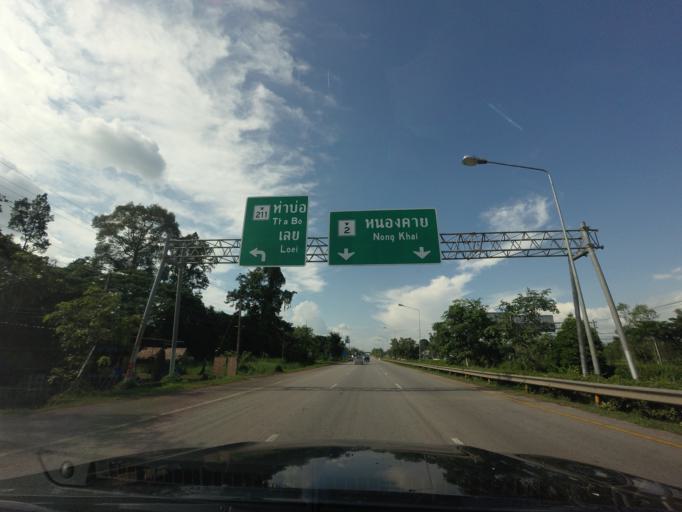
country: TH
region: Nong Khai
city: Sa Khrai
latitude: 17.7654
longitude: 102.7688
